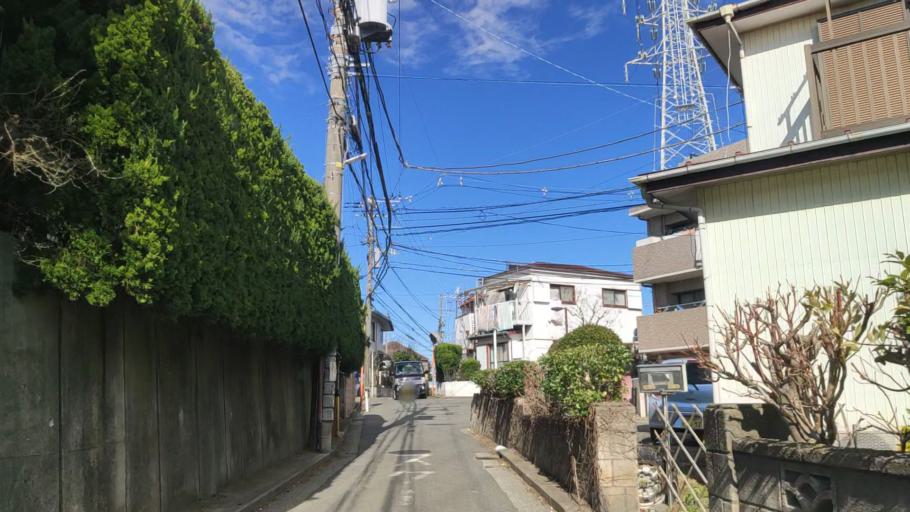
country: JP
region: Kanagawa
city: Yokohama
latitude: 35.4706
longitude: 139.5830
